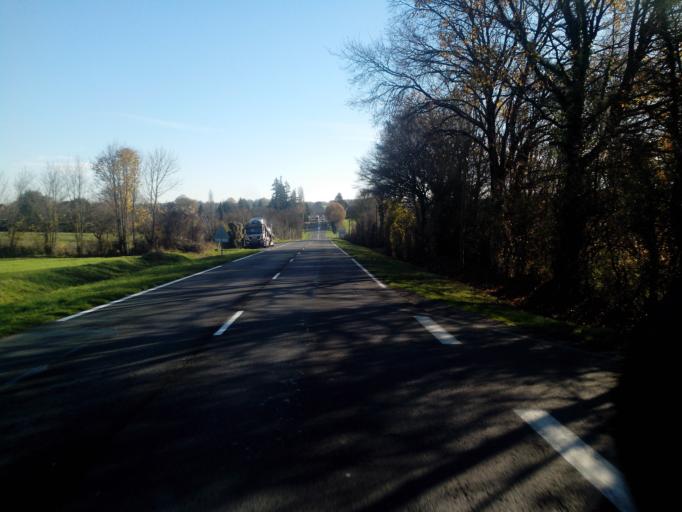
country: FR
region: Poitou-Charentes
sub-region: Departement de la Vienne
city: Terce
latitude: 46.4399
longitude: 0.5872
